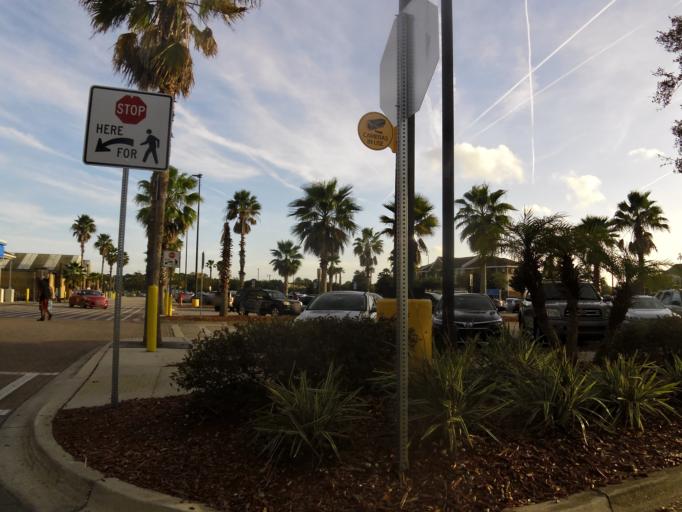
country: US
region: Florida
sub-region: Duval County
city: Jacksonville
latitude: 30.3418
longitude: -81.5460
